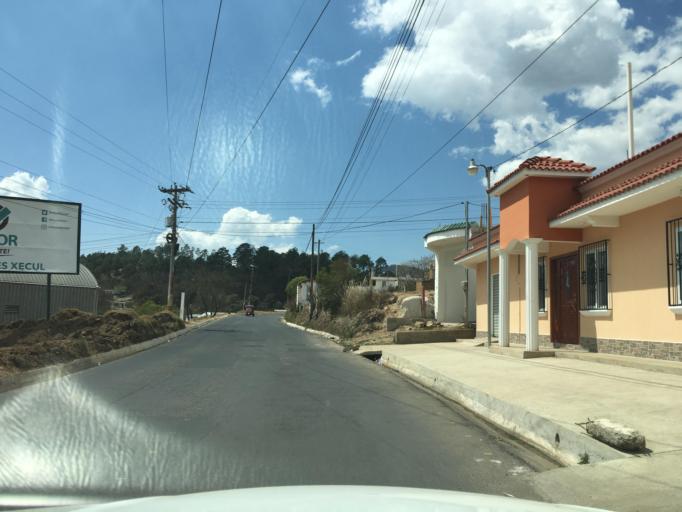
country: GT
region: Quetzaltenango
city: Salcaja
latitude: 14.9059
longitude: -91.4567
